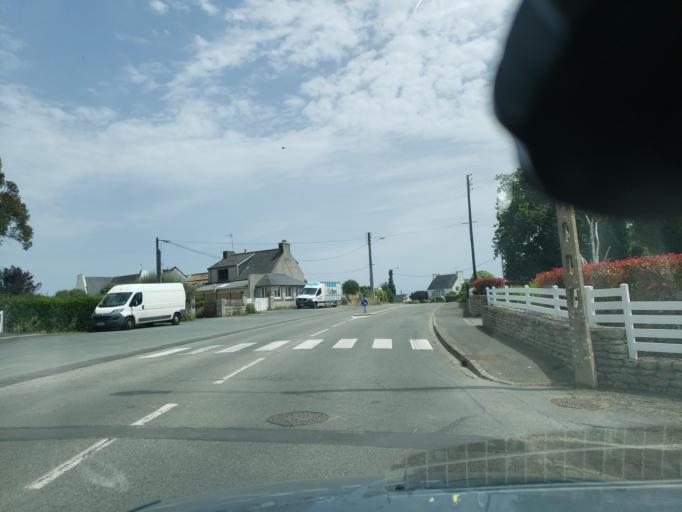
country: FR
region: Brittany
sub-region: Departement du Finistere
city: Treffiagat
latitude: 47.8013
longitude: -4.2602
